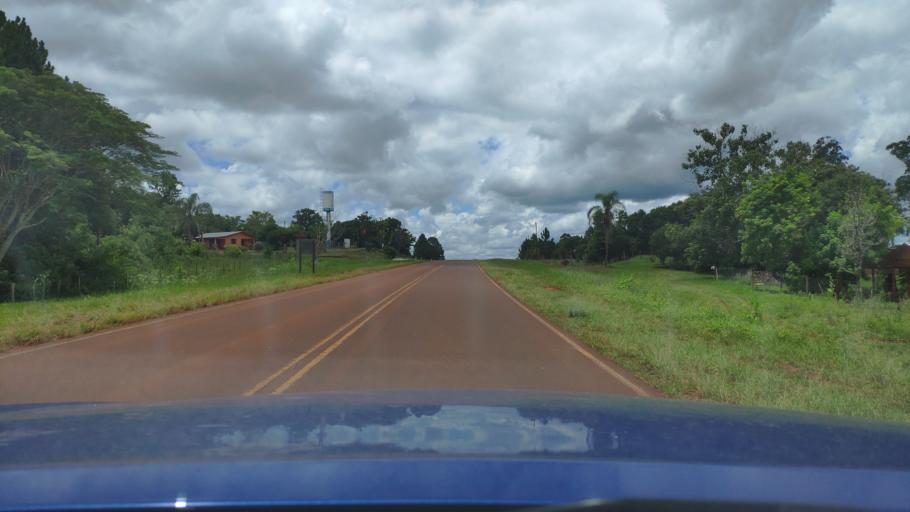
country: AR
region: Misiones
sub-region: Departamento de San Javier
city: San Javier
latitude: -27.8566
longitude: -55.2516
